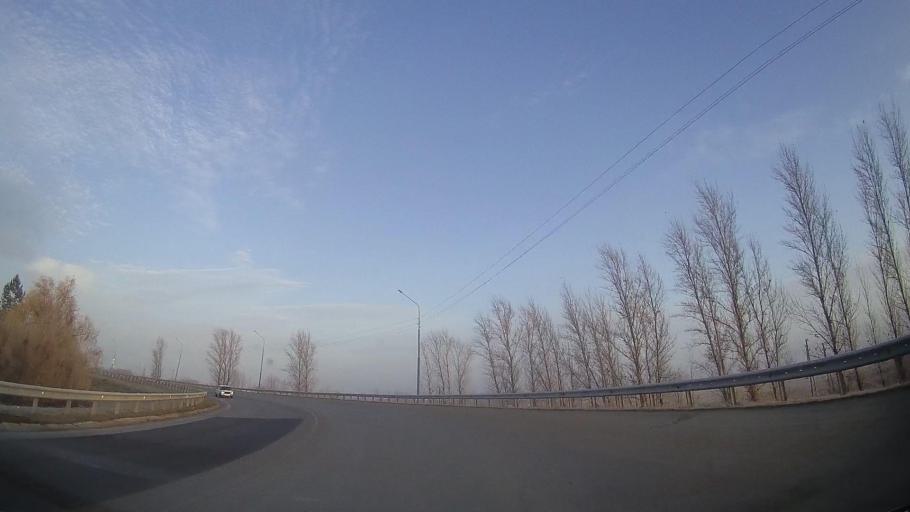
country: RU
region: Rostov
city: Bataysk
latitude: 47.1023
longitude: 39.7668
